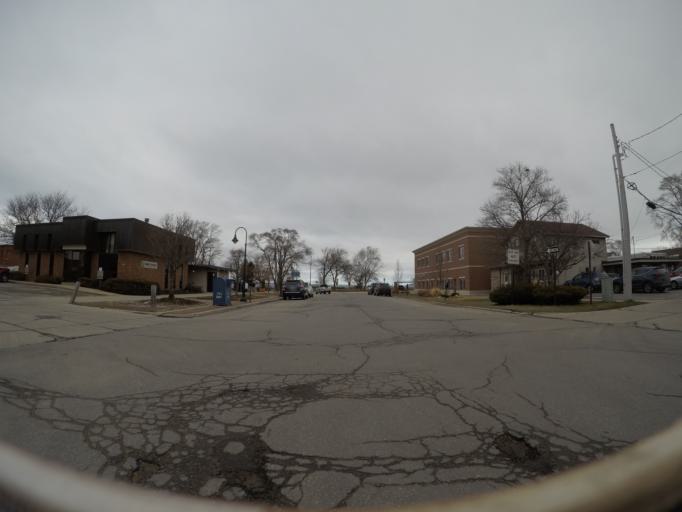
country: US
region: Michigan
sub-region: Grand Traverse County
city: Traverse City
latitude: 44.7635
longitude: -85.6159
